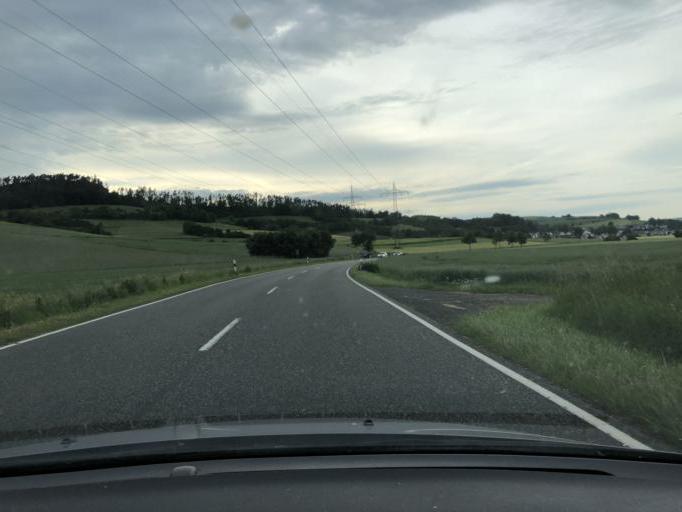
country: DE
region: Hesse
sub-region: Regierungsbezirk Kassel
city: Alheim
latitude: 51.0118
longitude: 9.6809
